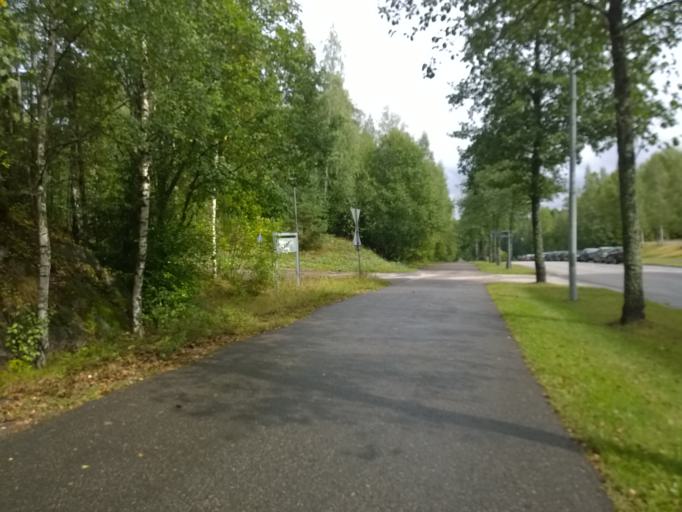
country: FI
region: Pirkanmaa
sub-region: Tampere
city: Tampere
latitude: 61.4486
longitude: 23.8638
